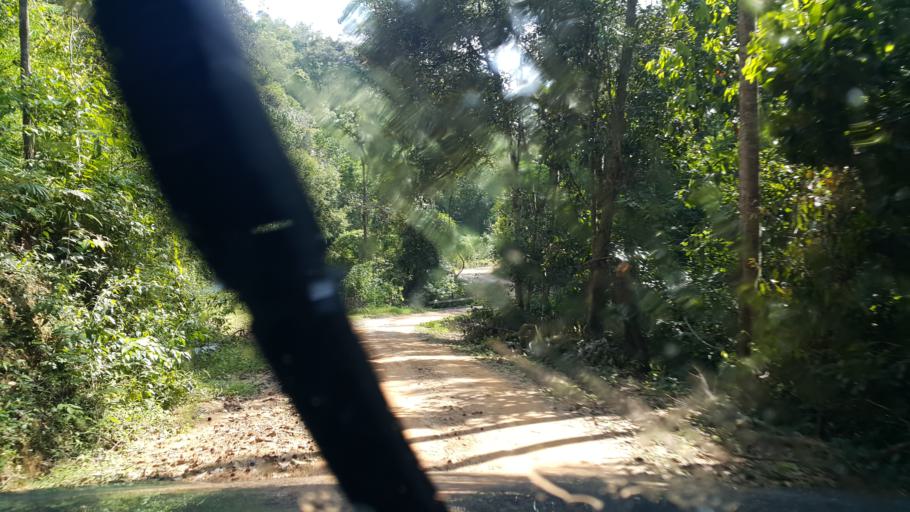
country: TH
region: Chiang Mai
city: Phrao
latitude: 19.0833
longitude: 99.2520
